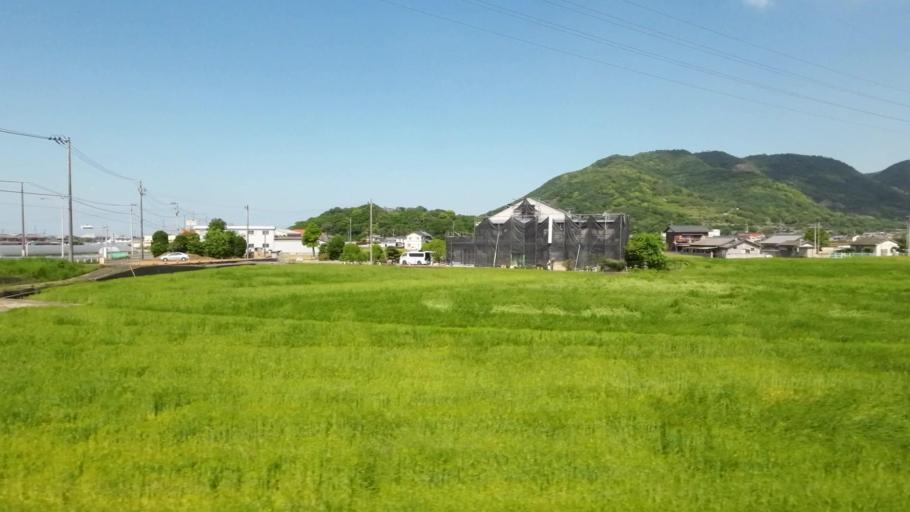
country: JP
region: Kagawa
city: Kan'onjicho
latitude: 34.1360
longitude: 133.6843
